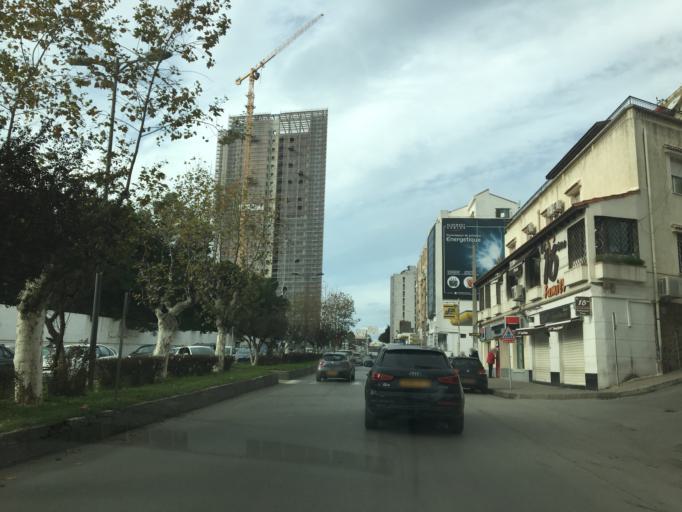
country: DZ
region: Alger
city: Algiers
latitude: 36.7689
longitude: 3.0228
